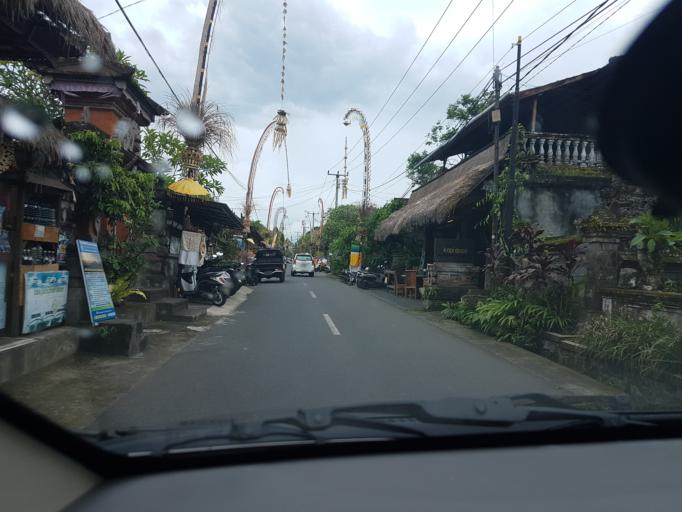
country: ID
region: Bali
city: Banjar Pande
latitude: -8.5055
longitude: 115.2476
